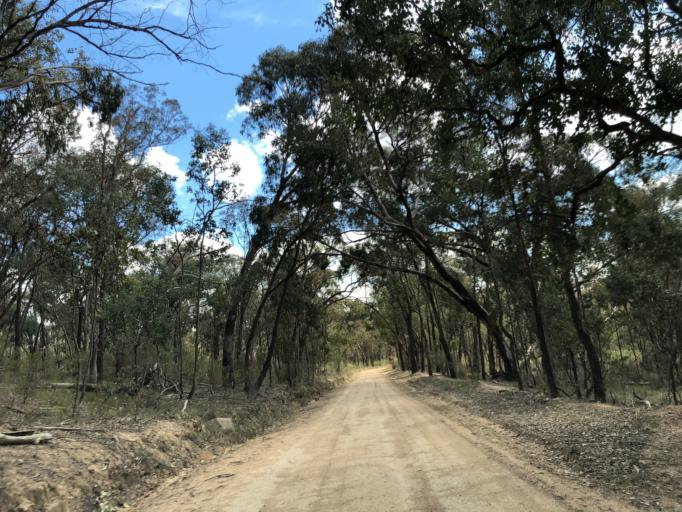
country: AU
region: Victoria
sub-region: Benalla
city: Benalla
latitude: -36.7388
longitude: 146.1532
